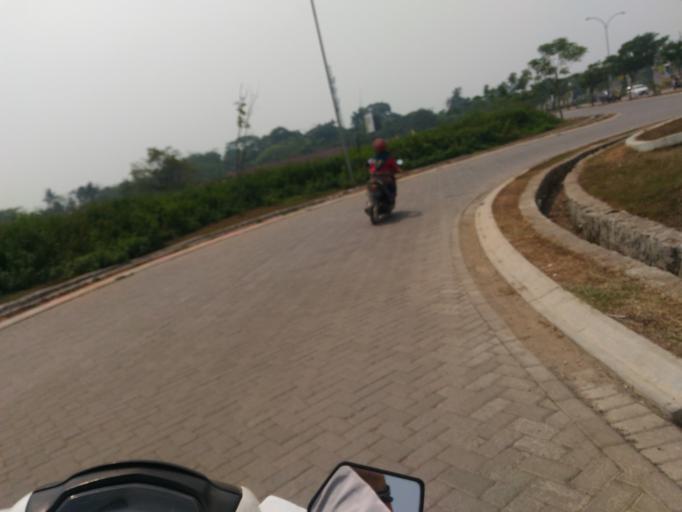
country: ID
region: West Java
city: Pasarkemis
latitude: -6.1398
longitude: 106.5409
